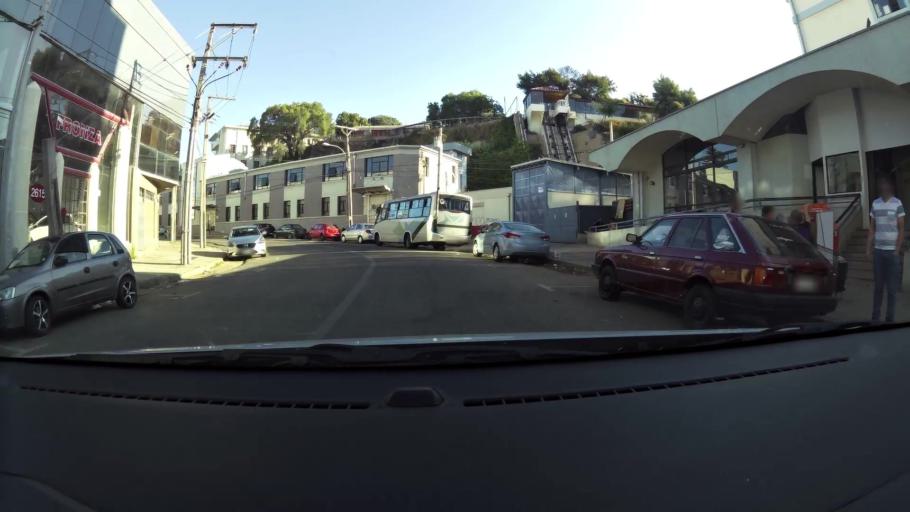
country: CL
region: Valparaiso
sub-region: Provincia de Valparaiso
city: Valparaiso
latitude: -33.0512
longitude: -71.6102
